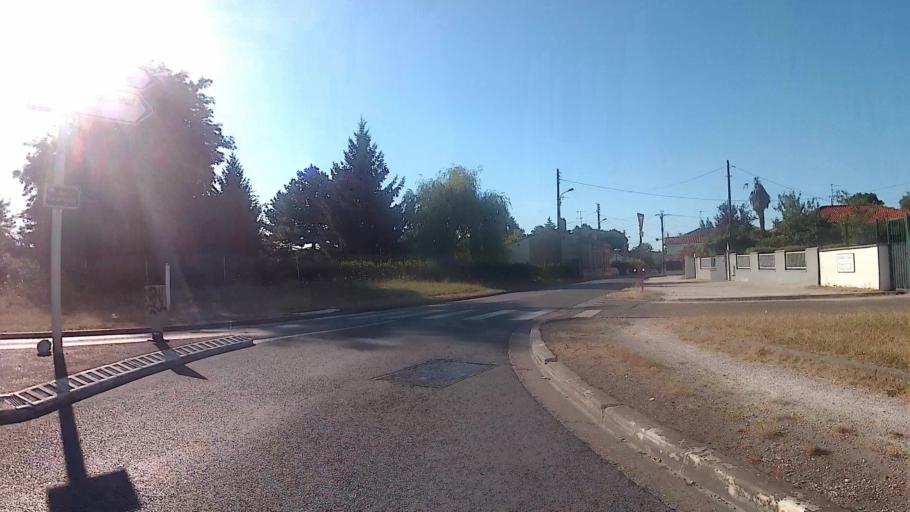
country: FR
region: Aquitaine
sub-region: Departement de la Gironde
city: Talence
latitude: 44.7807
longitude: -0.5757
